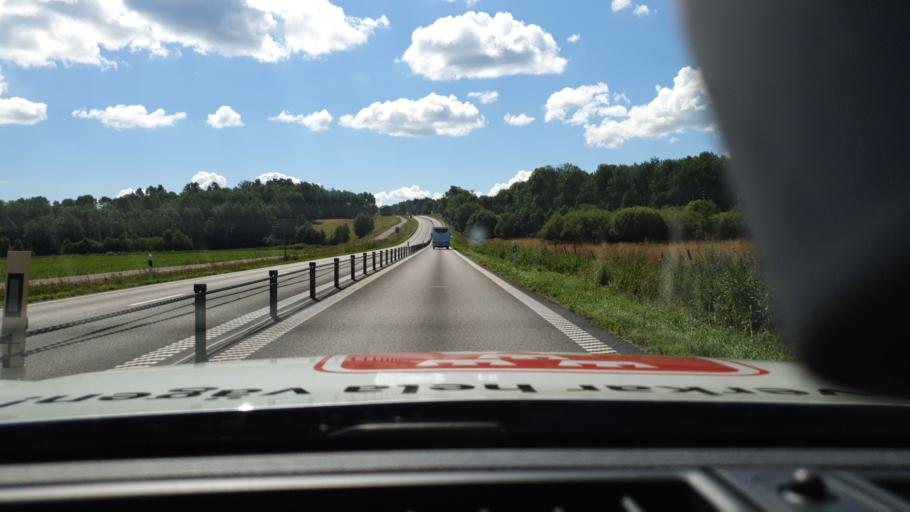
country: SE
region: Joenkoeping
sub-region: Tranas Kommun
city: Tranas
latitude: 57.9829
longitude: 14.9143
